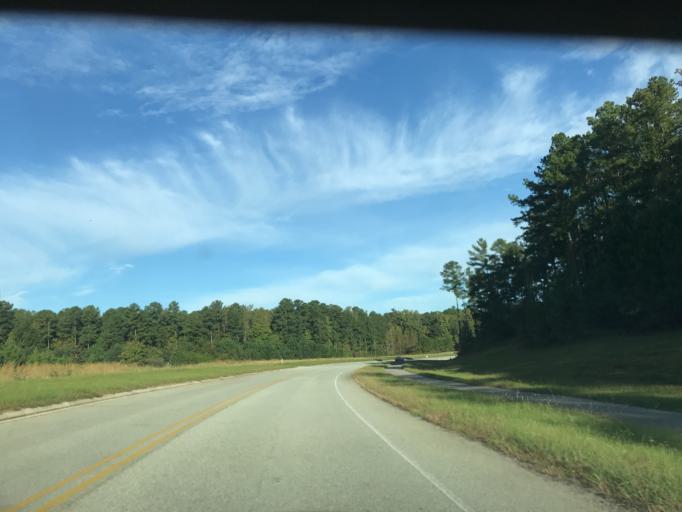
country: US
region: North Carolina
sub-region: Wake County
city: Morrisville
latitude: 35.8519
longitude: -78.8874
